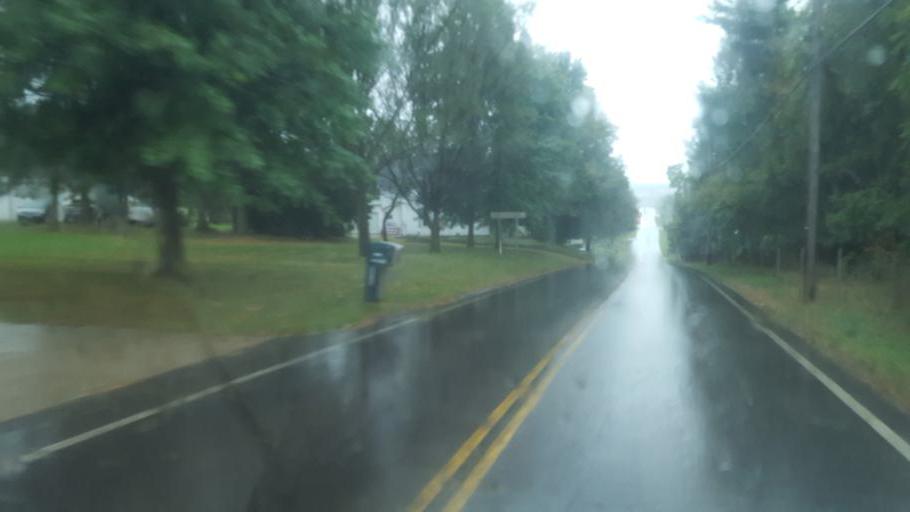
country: US
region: Ohio
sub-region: Richland County
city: Lincoln Heights
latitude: 40.7866
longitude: -82.4976
